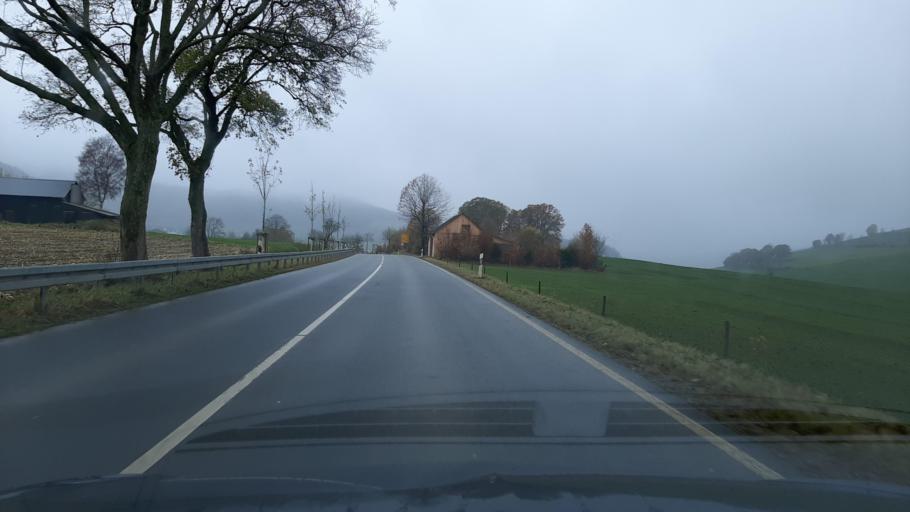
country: DE
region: North Rhine-Westphalia
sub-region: Regierungsbezirk Arnsberg
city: Bad Fredeburg
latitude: 51.2487
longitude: 8.4073
